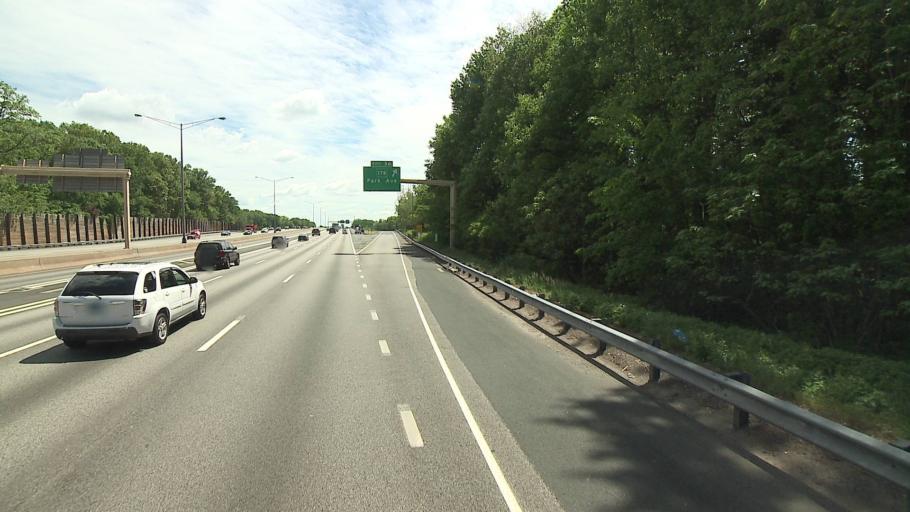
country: US
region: Connecticut
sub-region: Hartford County
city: Windsor
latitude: 41.8427
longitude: -72.6653
